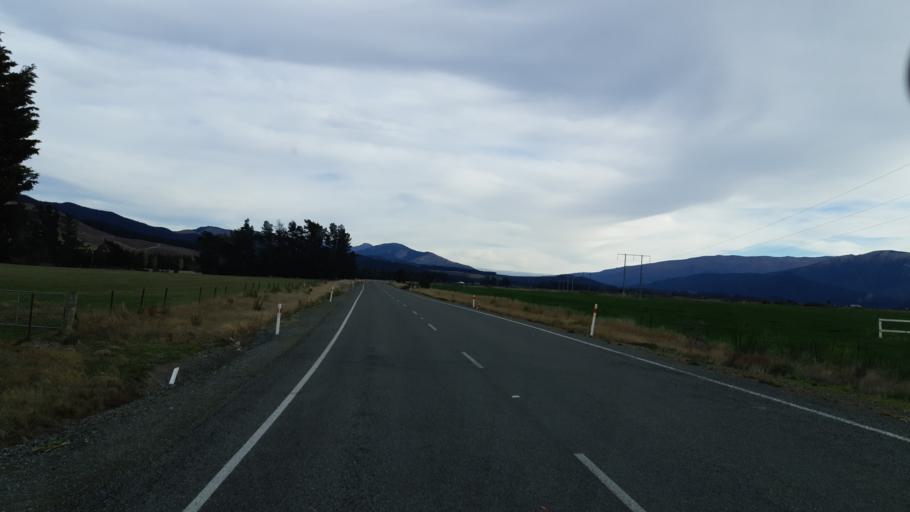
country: NZ
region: Tasman
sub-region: Tasman District
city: Brightwater
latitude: -41.6436
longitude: 173.3007
